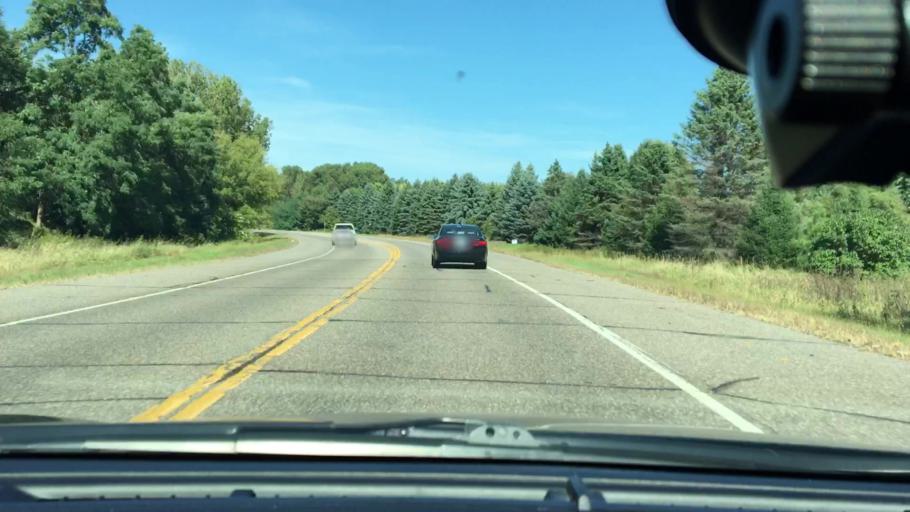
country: US
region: Minnesota
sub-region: Washington County
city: Mahtomedi
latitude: 45.0489
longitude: -92.9483
